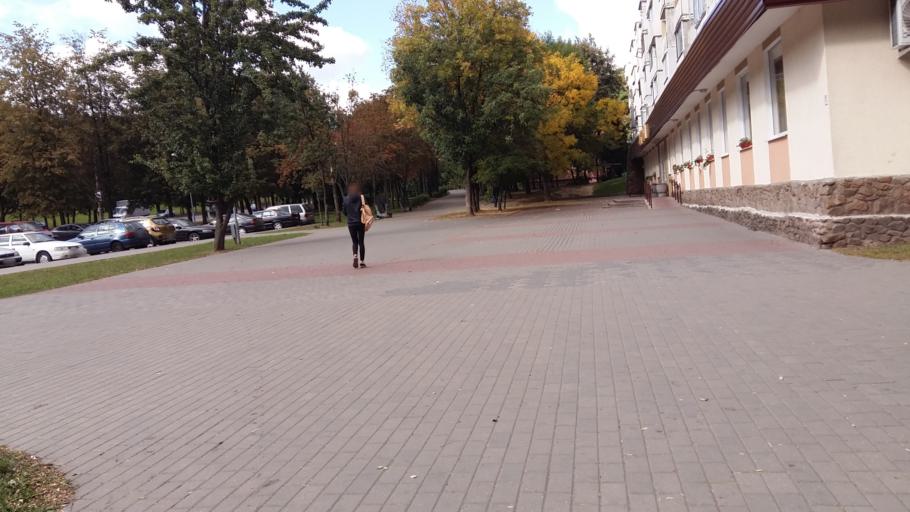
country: BY
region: Grodnenskaya
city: Hrodna
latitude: 53.6976
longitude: 23.8011
